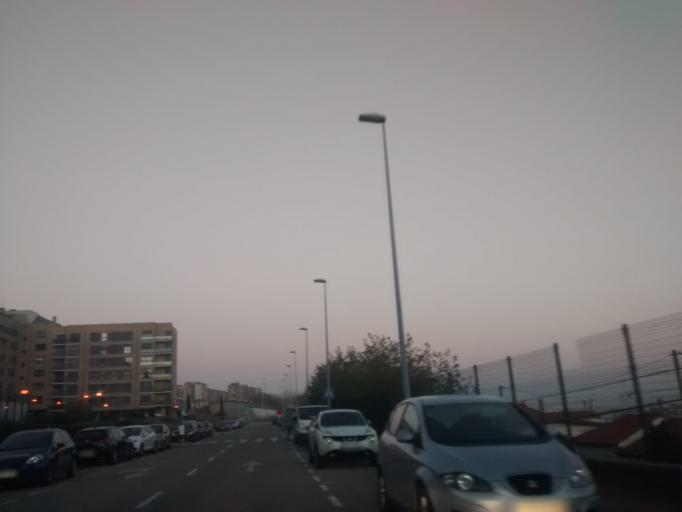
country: ES
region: Cantabria
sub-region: Provincia de Cantabria
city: Santander
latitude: 43.4545
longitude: -3.8508
